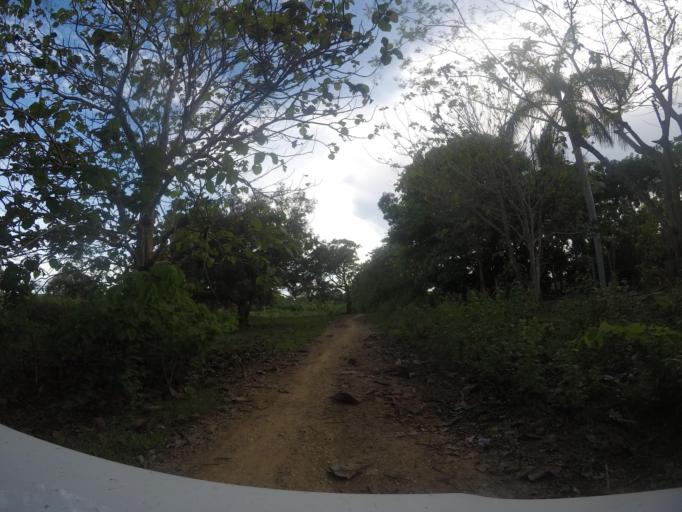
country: TL
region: Lautem
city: Lospalos
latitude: -8.5104
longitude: 126.9931
